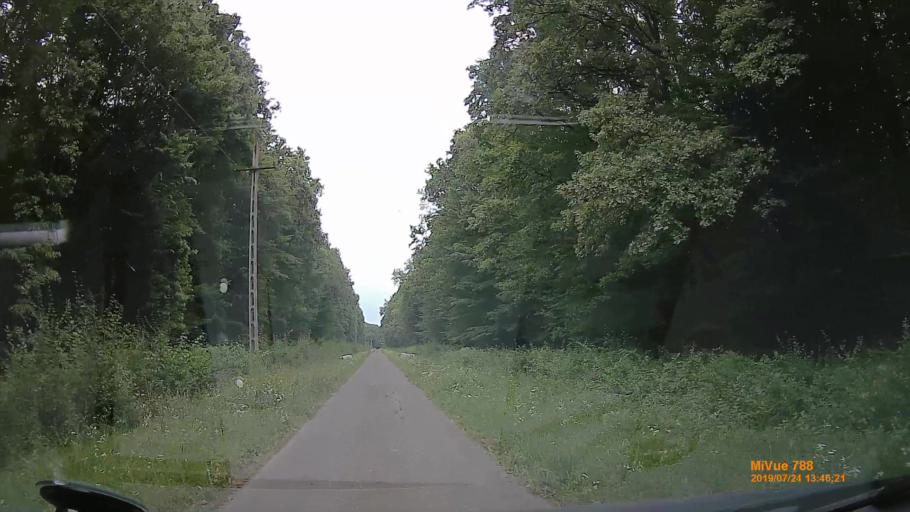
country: HU
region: Szabolcs-Szatmar-Bereg
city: Aranyosapati
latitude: 48.2662
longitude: 22.3409
